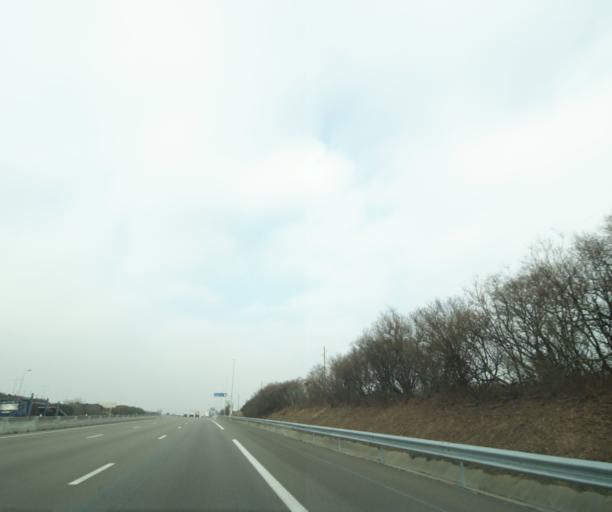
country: FR
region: Rhone-Alpes
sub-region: Departement de la Drome
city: La Roche-de-Glun
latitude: 45.0153
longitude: 4.8761
